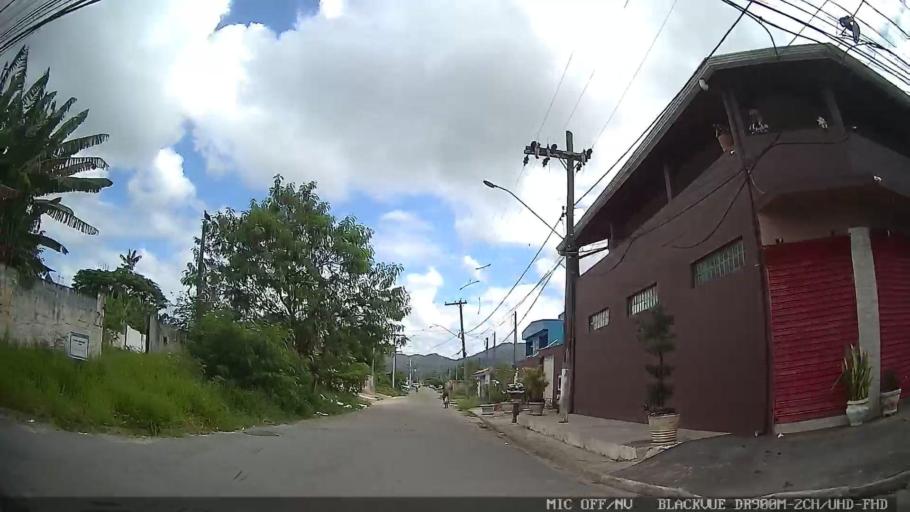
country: BR
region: Sao Paulo
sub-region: Peruibe
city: Peruibe
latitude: -24.2984
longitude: -47.0241
